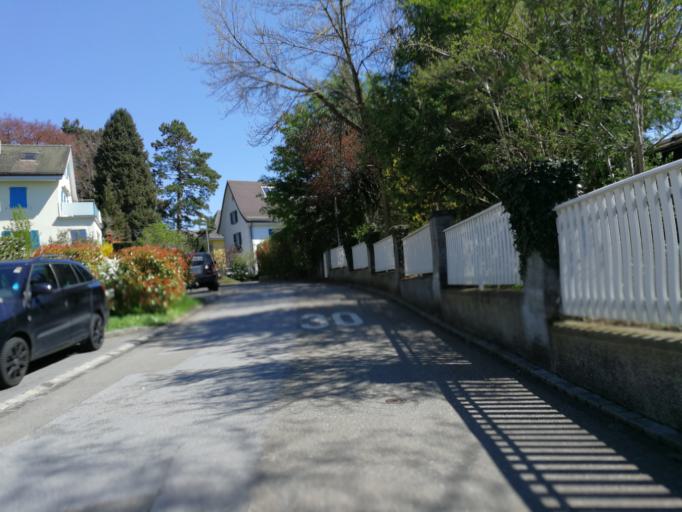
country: CH
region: Zurich
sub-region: Bezirk Meilen
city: Uetikon
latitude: 47.2619
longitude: 8.6815
